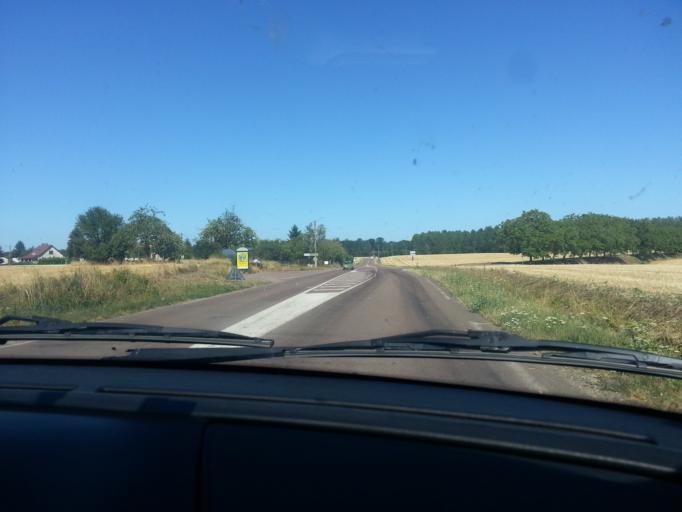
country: FR
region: Bourgogne
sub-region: Departement de Saone-et-Loire
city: Saint-Martin-en-Bresse
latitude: 46.8018
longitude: 4.9923
